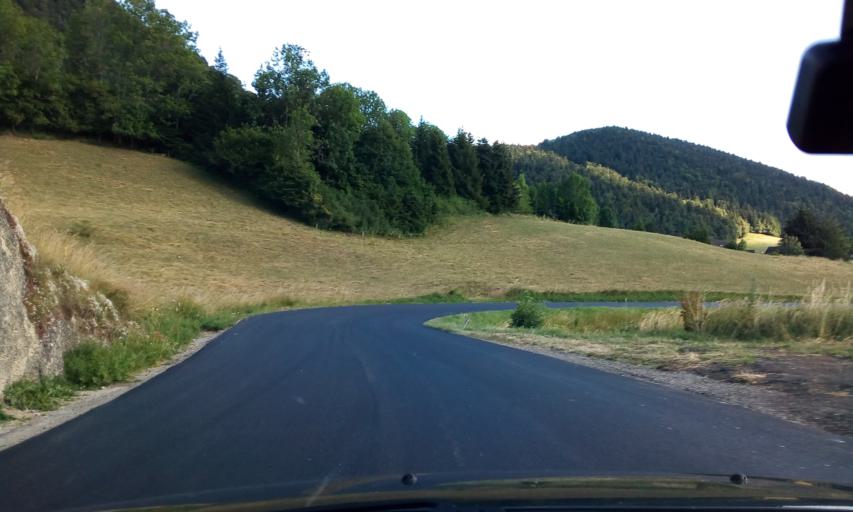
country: FR
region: Rhone-Alpes
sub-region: Departement de l'Isere
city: Lans-en-Vercors
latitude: 45.1311
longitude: 5.6010
